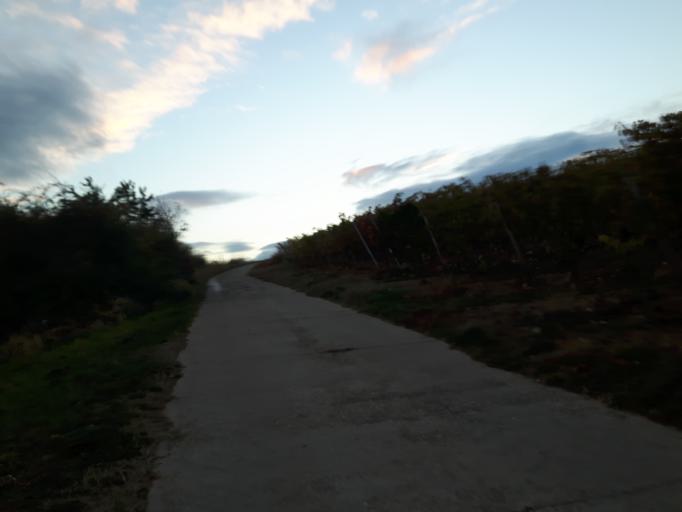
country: DE
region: Rheinland-Pfalz
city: Molsheim
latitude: 49.6594
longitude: 8.1890
